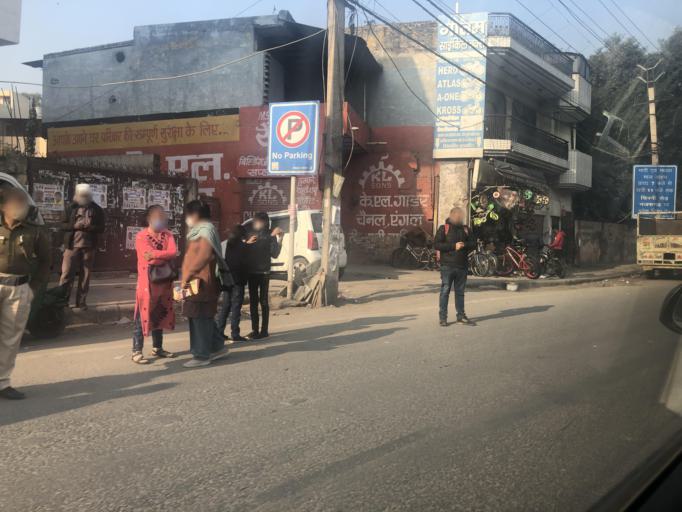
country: IN
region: Haryana
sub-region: Jhajjar
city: Bahadurgarh
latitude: 28.6143
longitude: 76.9810
